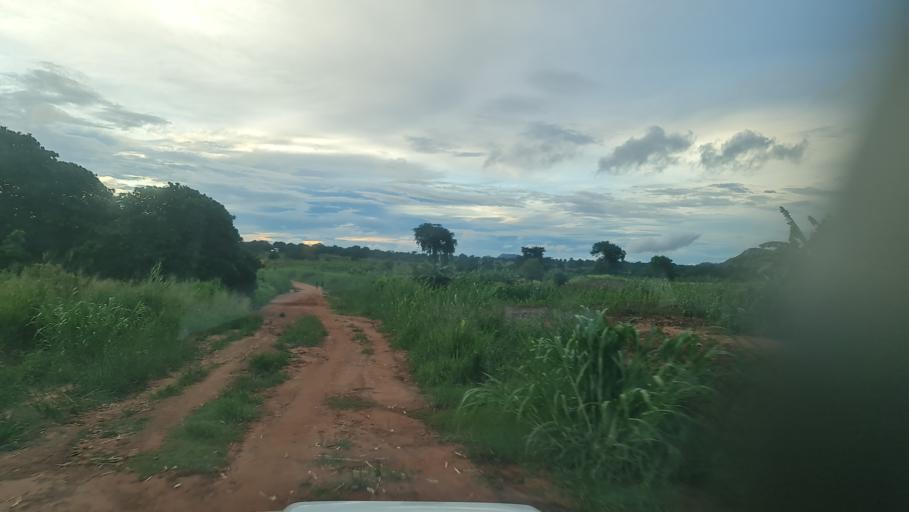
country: MZ
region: Nampula
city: Nacala
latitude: -14.7424
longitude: 39.9496
